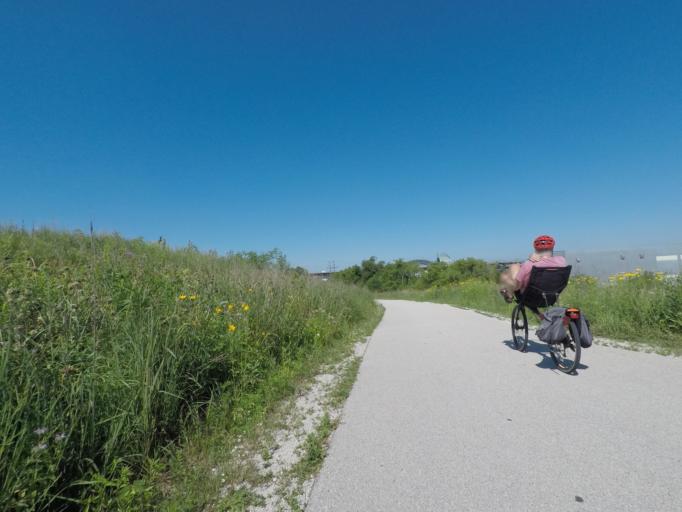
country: US
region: Wisconsin
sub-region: Milwaukee County
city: West Milwaukee
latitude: 43.0261
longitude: -87.9525
